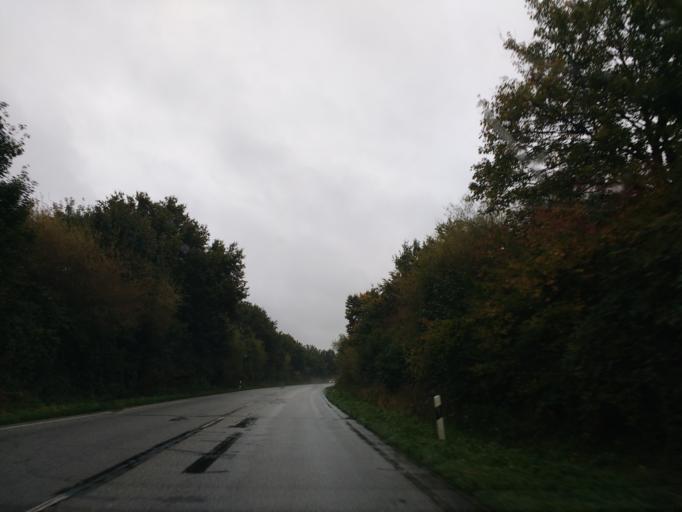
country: DE
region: Schleswig-Holstein
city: Susel
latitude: 54.0716
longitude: 10.7099
